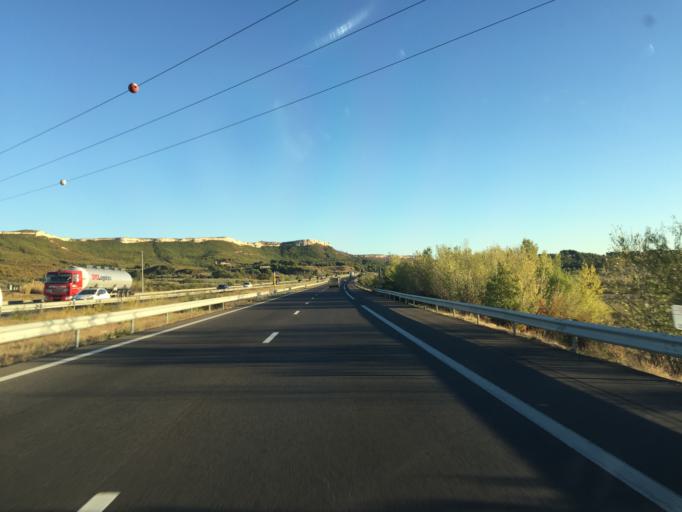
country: FR
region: Provence-Alpes-Cote d'Azur
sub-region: Departement des Bouches-du-Rhone
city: Rognac
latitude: 43.5089
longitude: 5.2353
